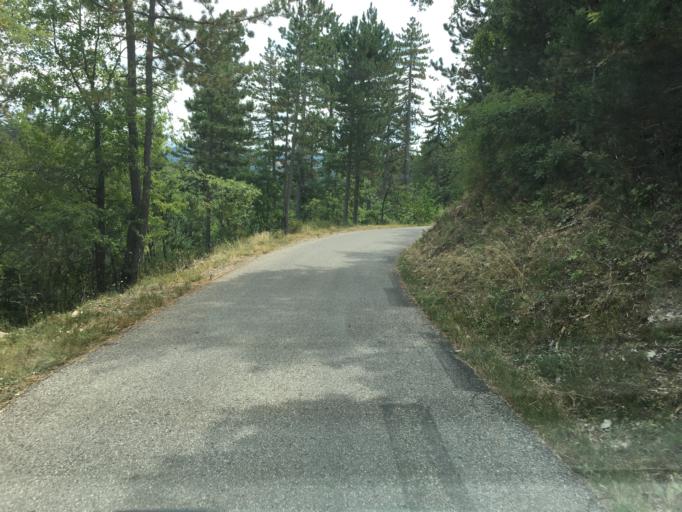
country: FR
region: Provence-Alpes-Cote d'Azur
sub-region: Departement des Alpes-de-Haute-Provence
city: Digne-les-Bains
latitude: 44.2126
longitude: 6.1490
